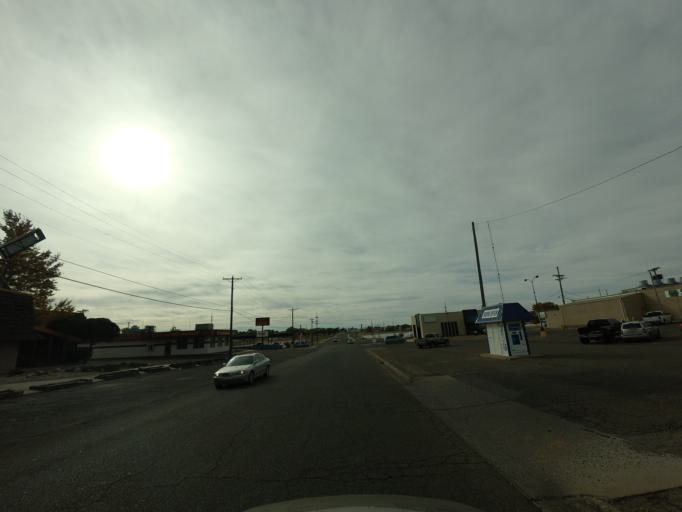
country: US
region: New Mexico
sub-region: Curry County
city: Clovis
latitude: 34.4205
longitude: -103.2054
